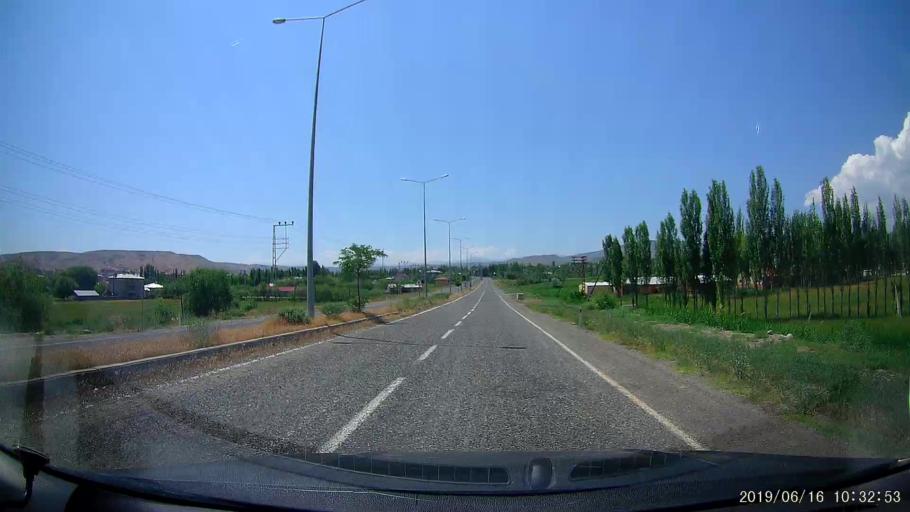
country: TR
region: Igdir
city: Tuzluca
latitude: 40.0469
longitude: 43.6532
